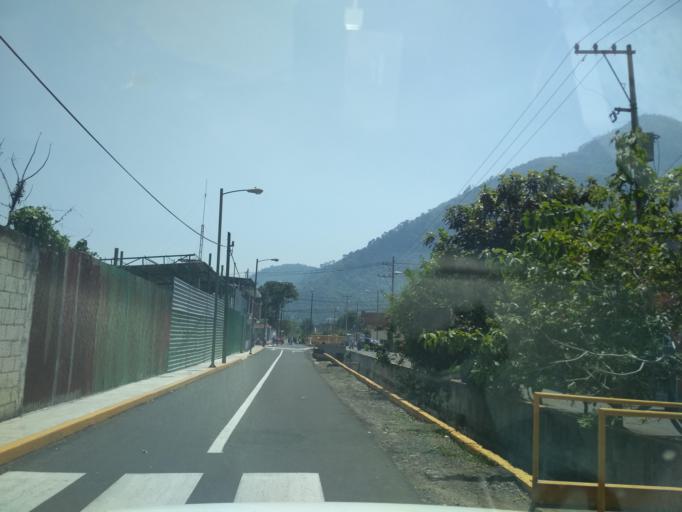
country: MX
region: Veracruz
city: Rio Blanco
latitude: 18.8358
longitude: -97.1115
